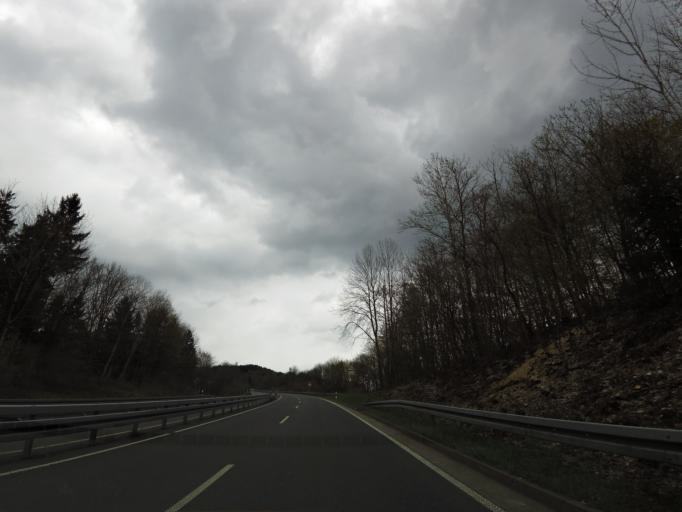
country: DE
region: Lower Saxony
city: Osterode am Harz
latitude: 51.7554
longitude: 10.2899
